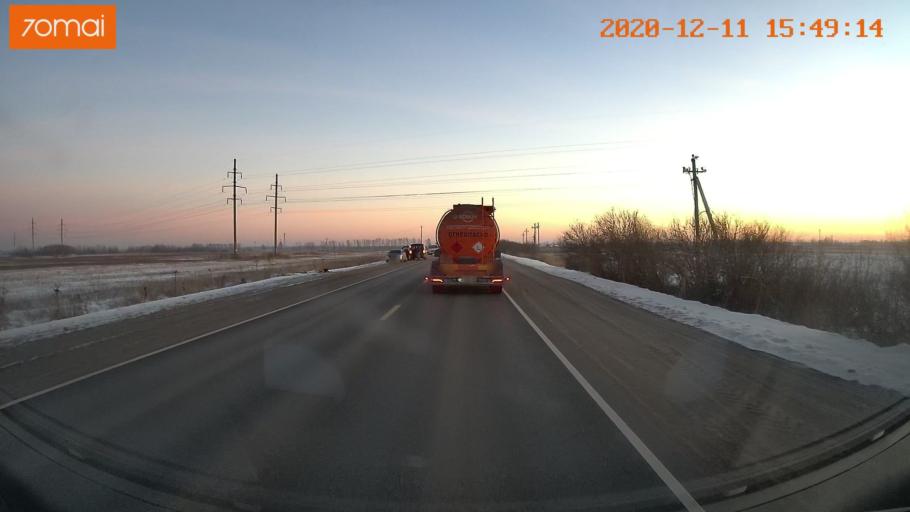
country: RU
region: Ivanovo
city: Novo-Talitsy
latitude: 56.9892
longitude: 40.8731
